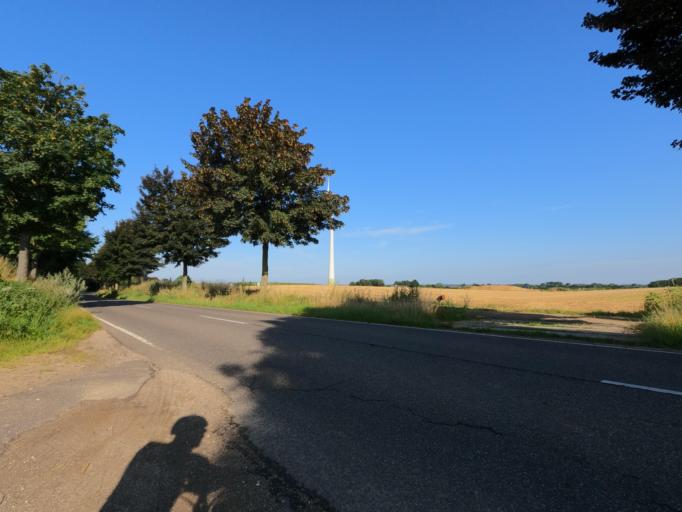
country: DE
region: North Rhine-Westphalia
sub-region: Regierungsbezirk Dusseldorf
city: Juchen
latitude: 51.0947
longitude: 6.4282
